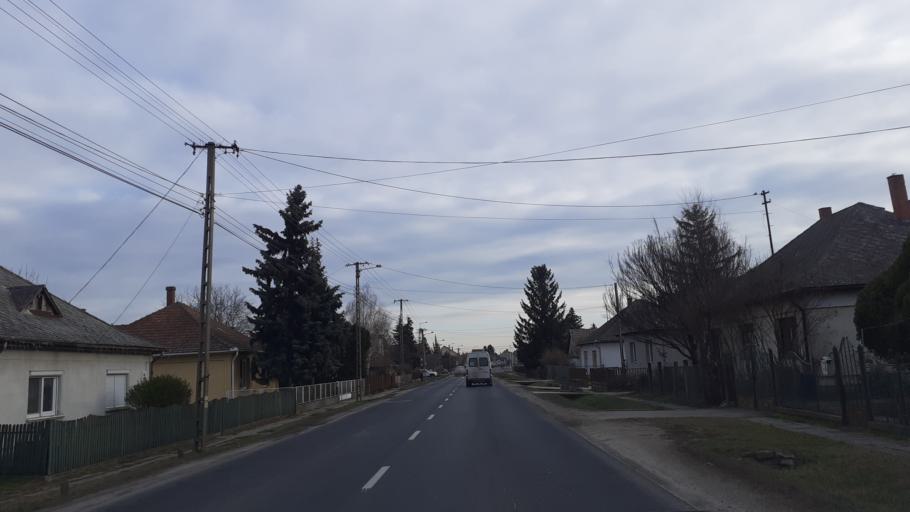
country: HU
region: Fejer
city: Sarbogard
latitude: 46.8642
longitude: 18.6286
